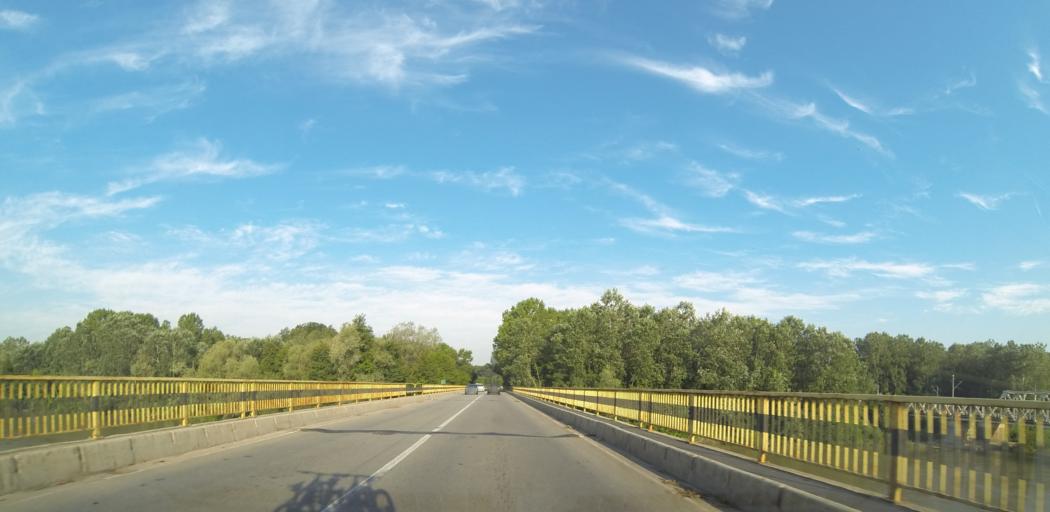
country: RO
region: Dolj
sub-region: Comuna Filiasi
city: Balta
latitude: 44.5684
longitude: 23.4556
